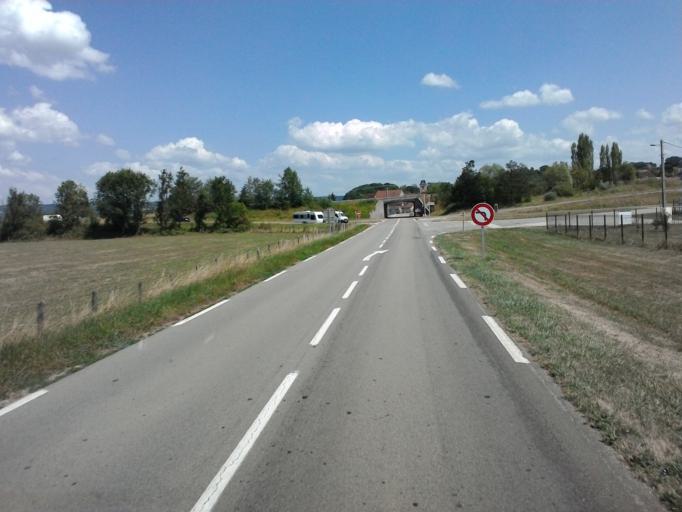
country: FR
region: Franche-Comte
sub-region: Departement du Jura
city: Montmorot
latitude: 46.7600
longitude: 5.5542
